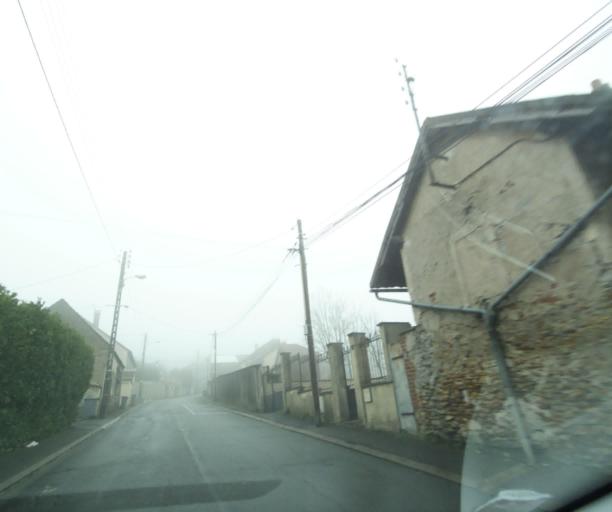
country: FR
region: Ile-de-France
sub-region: Departement de Seine-et-Marne
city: Dammartin-en-Goele
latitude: 49.0519
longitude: 2.6786
